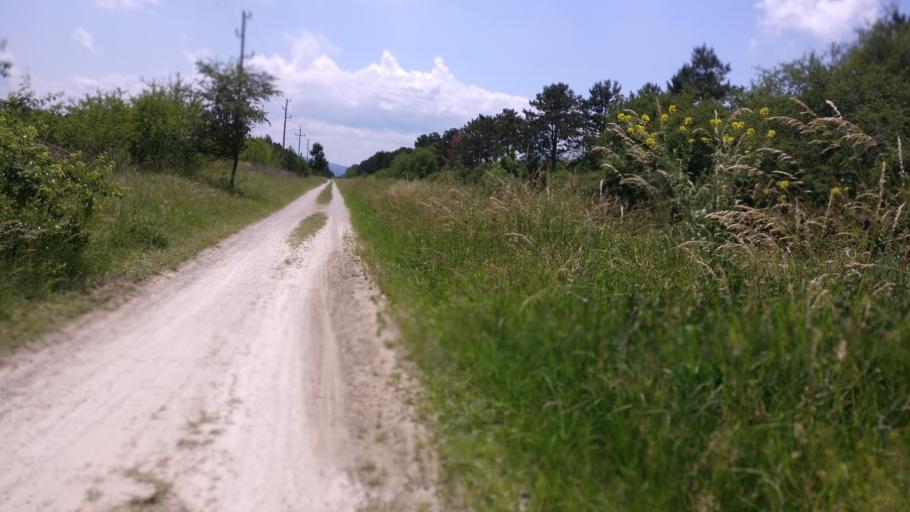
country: AT
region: Lower Austria
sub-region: Politischer Bezirk Wiener Neustadt
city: Lichtenworth
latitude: 47.8669
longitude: 16.2816
